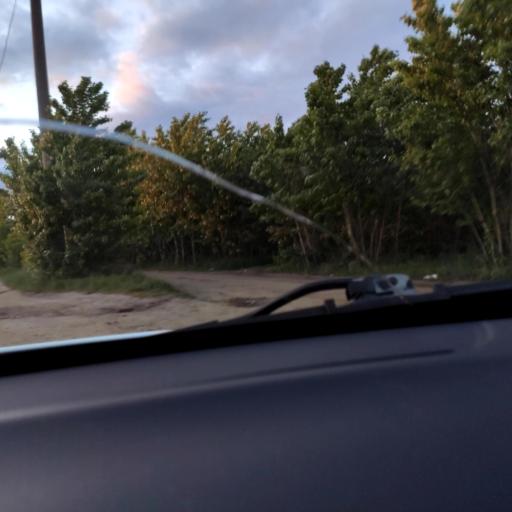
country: RU
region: Tatarstan
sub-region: Gorod Kazan'
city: Kazan
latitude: 55.7838
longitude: 49.0980
